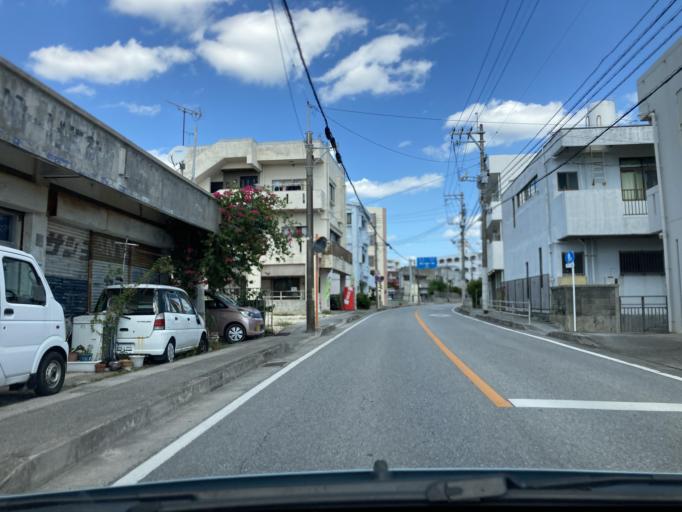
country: JP
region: Okinawa
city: Tomigusuku
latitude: 26.1873
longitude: 127.7275
